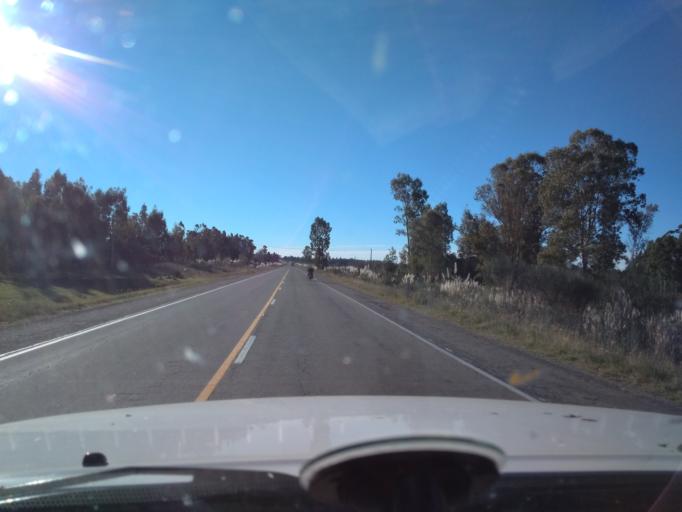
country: UY
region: Canelones
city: Sauce
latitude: -34.6067
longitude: -56.0486
